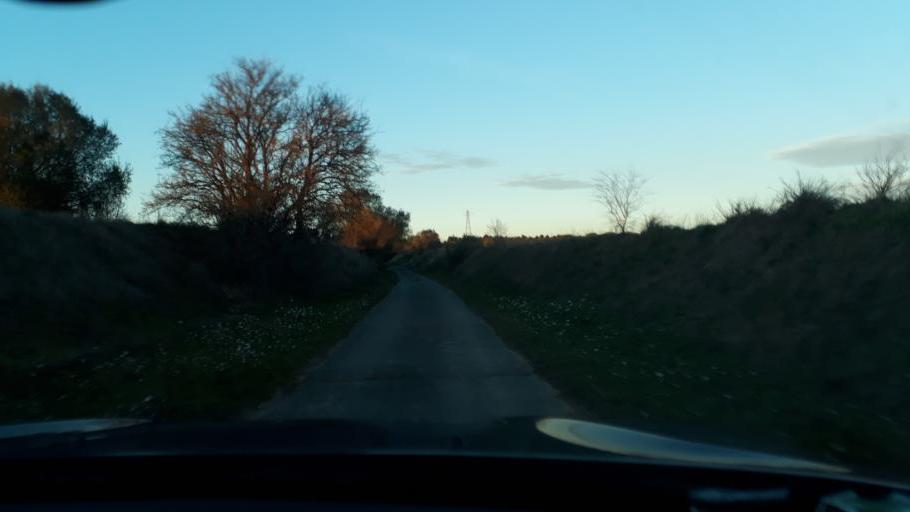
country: FR
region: Languedoc-Roussillon
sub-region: Departement de l'Herault
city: Florensac
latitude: 43.4061
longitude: 3.4603
